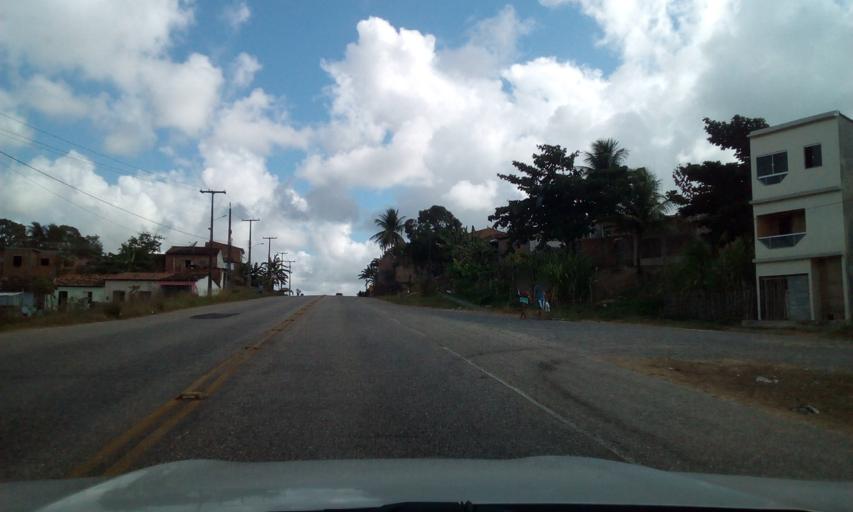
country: BR
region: Sergipe
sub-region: Estancia
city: Estancia
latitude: -11.3540
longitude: -37.4504
